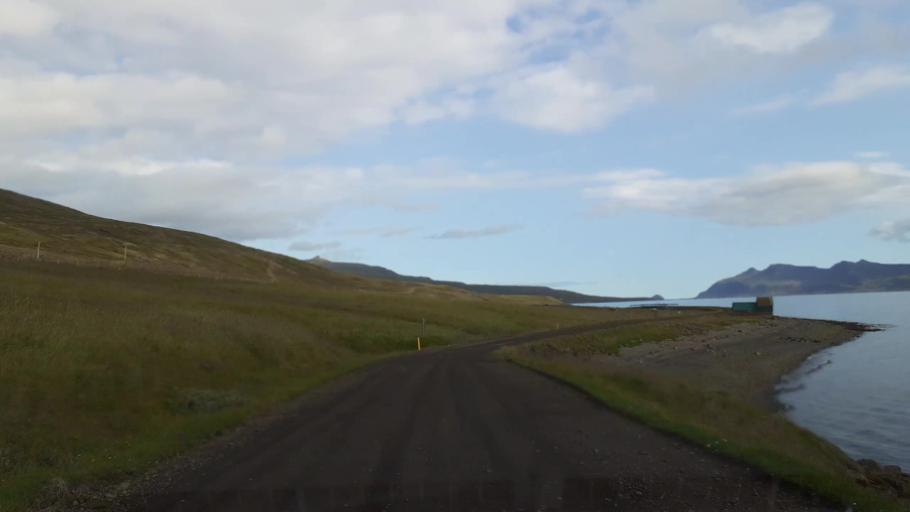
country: IS
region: East
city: Eskifjoerdur
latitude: 65.0376
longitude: -13.8772
